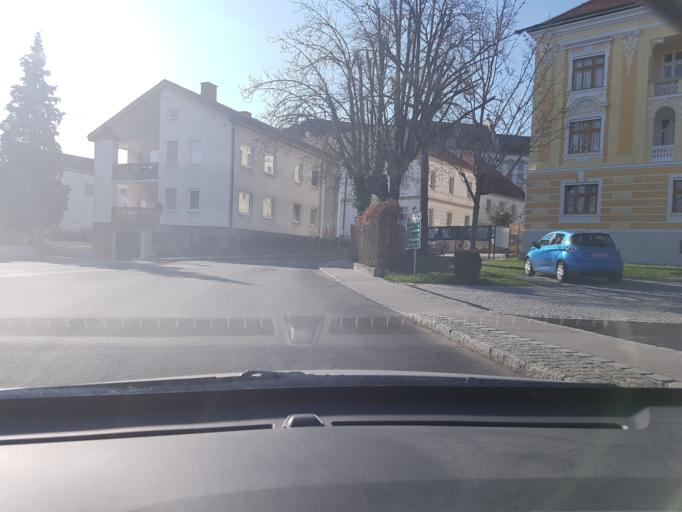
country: AT
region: Upper Austria
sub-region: Politischer Bezirk Linz-Land
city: Sankt Florian
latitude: 48.2059
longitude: 14.3816
